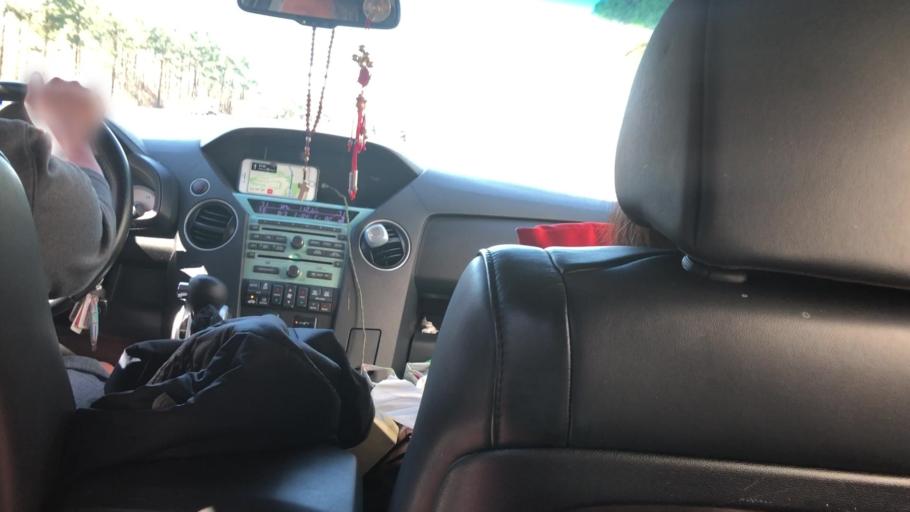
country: US
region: Louisiana
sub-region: Saint John the Baptist Parish
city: Laplace
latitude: 30.1014
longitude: -90.4846
